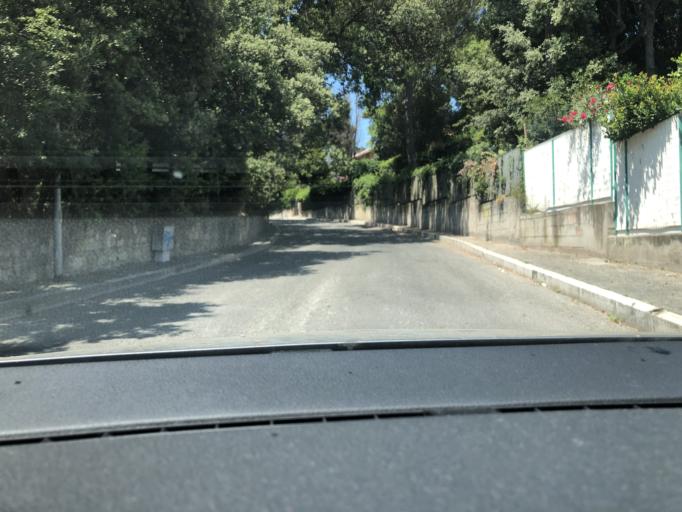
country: IT
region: Latium
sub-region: Citta metropolitana di Roma Capitale
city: Nettuno
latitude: 41.4567
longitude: 12.6478
